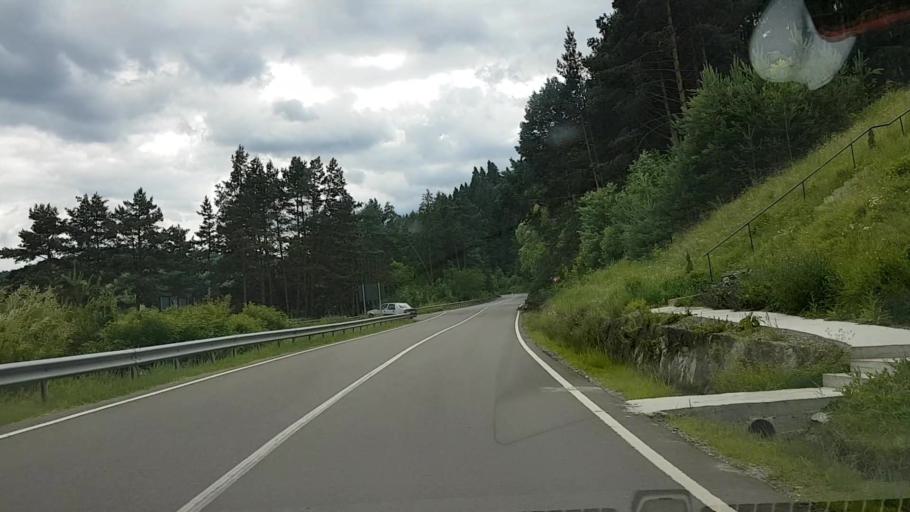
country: RO
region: Neamt
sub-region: Comuna Poiana Teiului
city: Poiana Teiului
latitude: 47.0893
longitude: 25.9598
